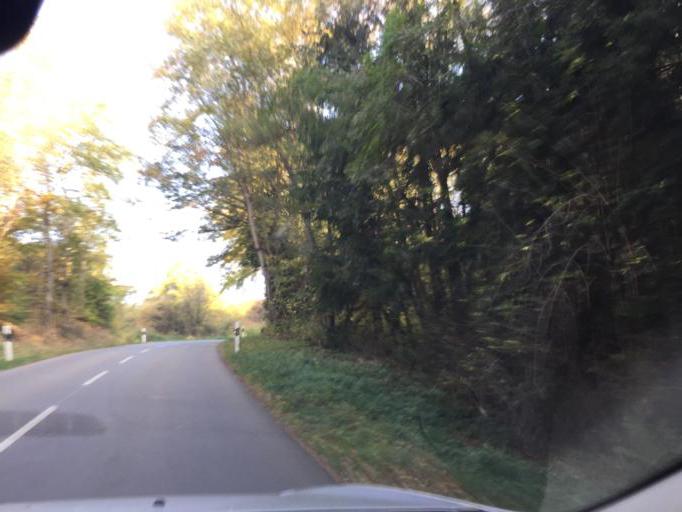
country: LU
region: Luxembourg
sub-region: Canton de Luxembourg
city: Contern
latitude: 49.5704
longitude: 6.2163
